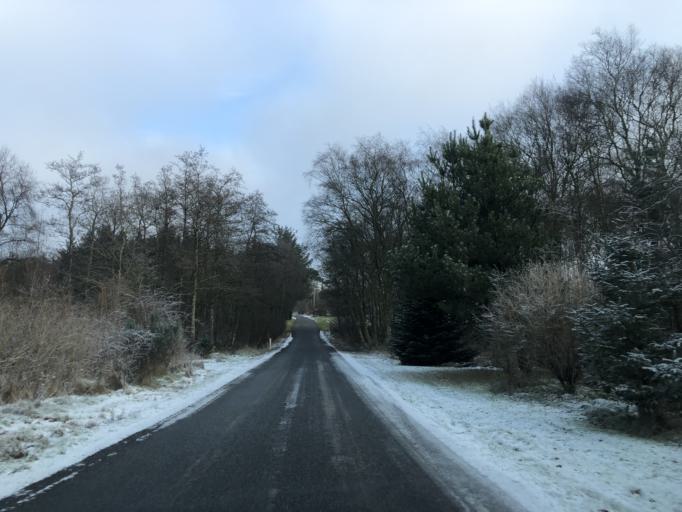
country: DK
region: Central Jutland
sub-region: Holstebro Kommune
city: Ulfborg
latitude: 56.2058
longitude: 8.3711
